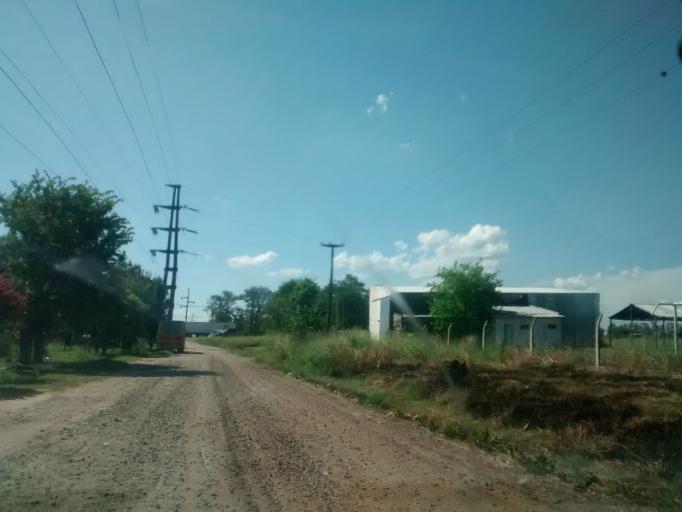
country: AR
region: Chaco
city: Fontana
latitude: -27.4034
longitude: -58.9973
